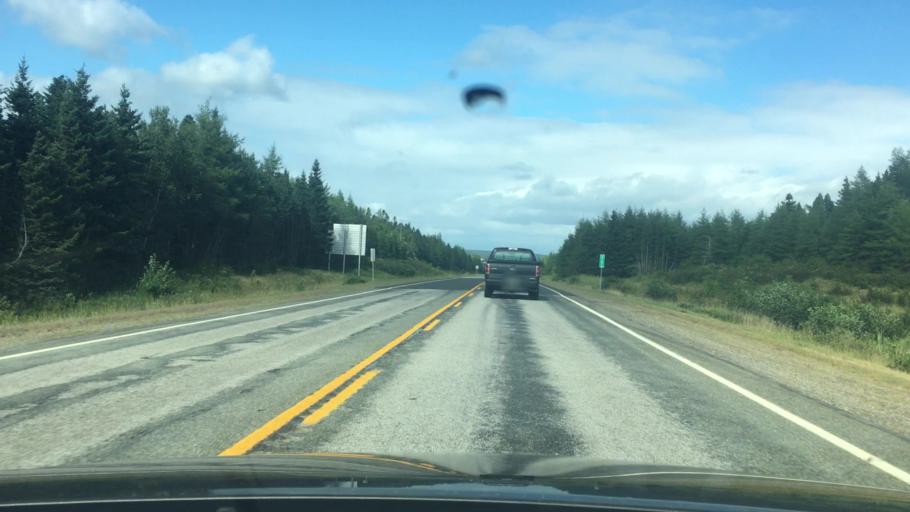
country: CA
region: Nova Scotia
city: Princeville
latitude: 45.6189
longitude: -61.0517
